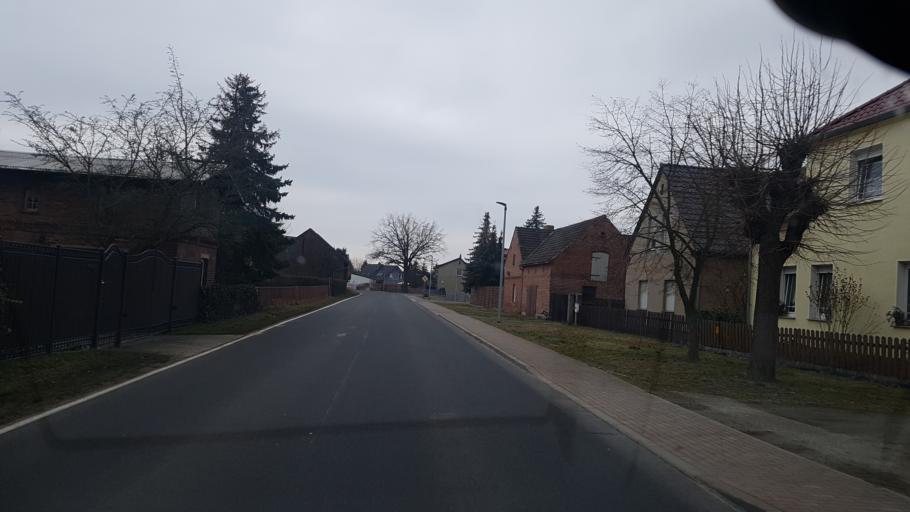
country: DE
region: Brandenburg
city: Heinersbruck
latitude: 51.7050
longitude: 14.4629
